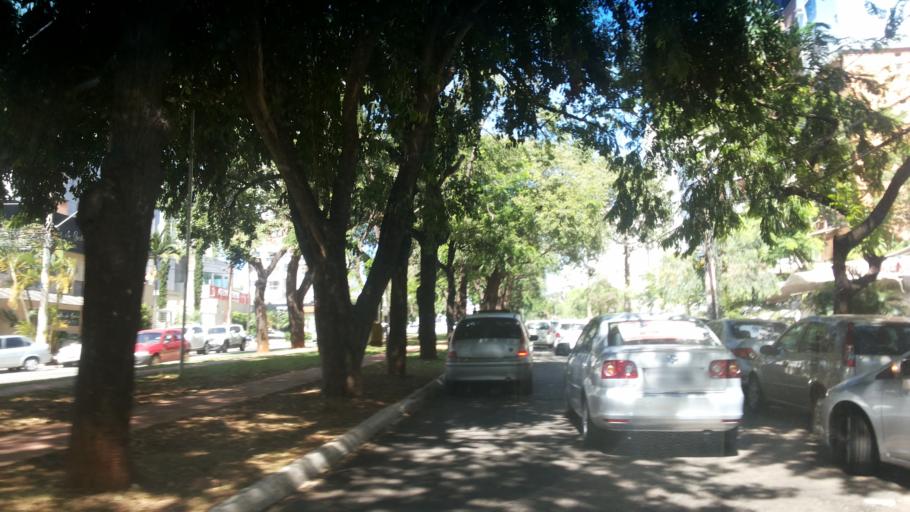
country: BR
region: Goias
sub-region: Goiania
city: Goiania
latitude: -16.7112
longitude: -49.2589
